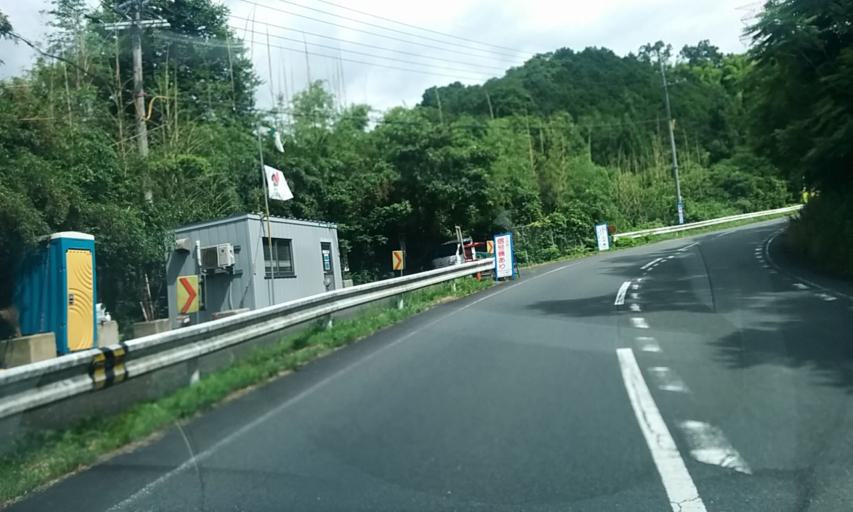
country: JP
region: Kyoto
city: Ayabe
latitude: 35.3518
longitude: 135.2730
